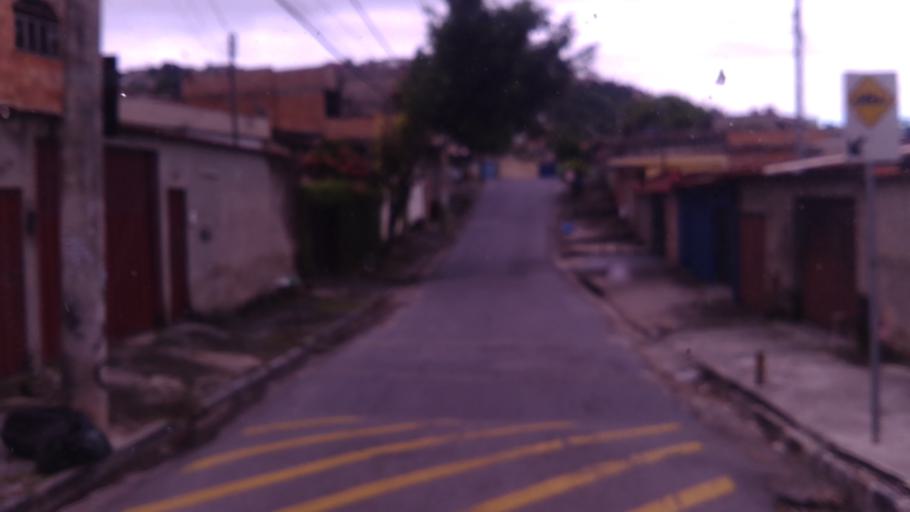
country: BR
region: Minas Gerais
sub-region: Santa Luzia
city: Santa Luzia
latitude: -19.8370
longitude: -43.9052
